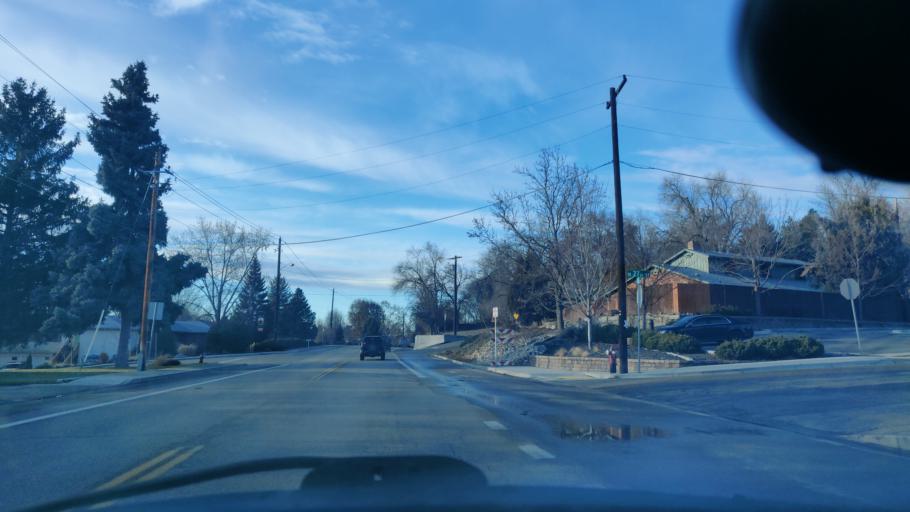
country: US
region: Idaho
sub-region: Ada County
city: Garden City
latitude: 43.6485
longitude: -116.2226
